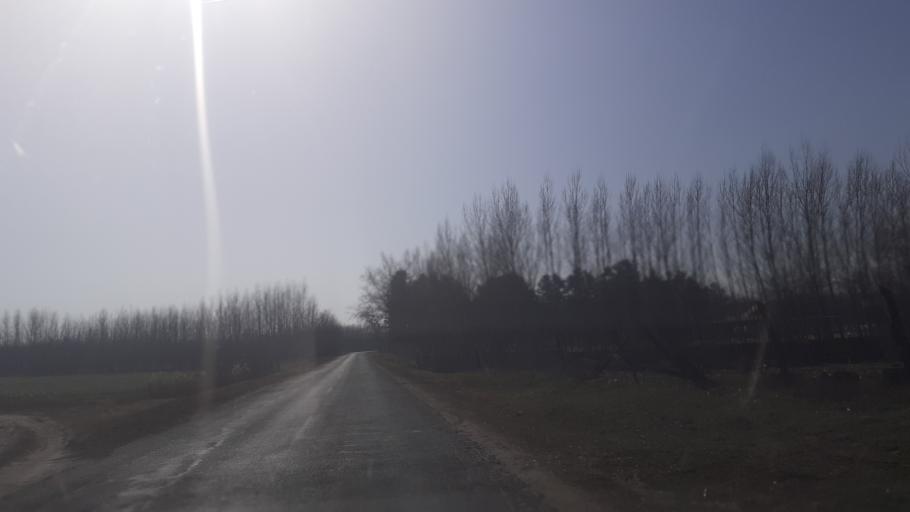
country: HU
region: Pest
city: Dabas
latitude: 47.1543
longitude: 19.3326
